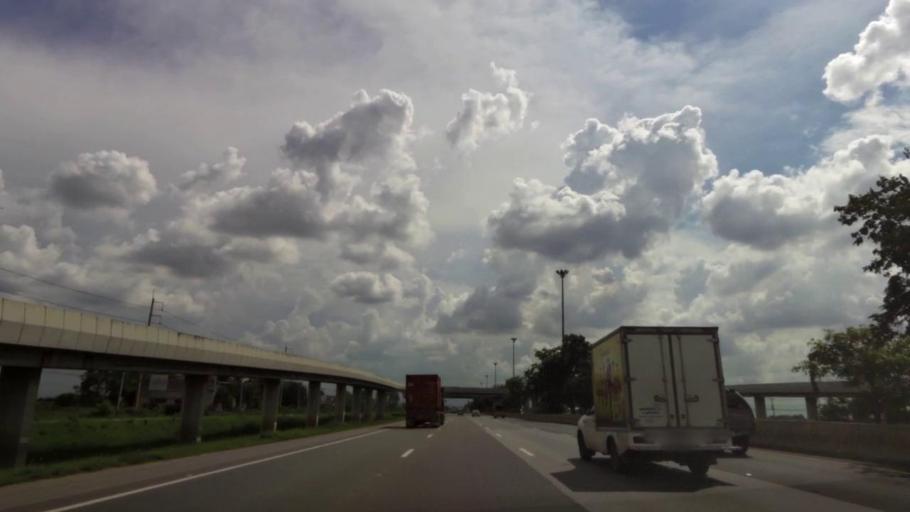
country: TH
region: Phra Nakhon Si Ayutthaya
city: Bang Pa-in
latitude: 14.2776
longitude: 100.6135
